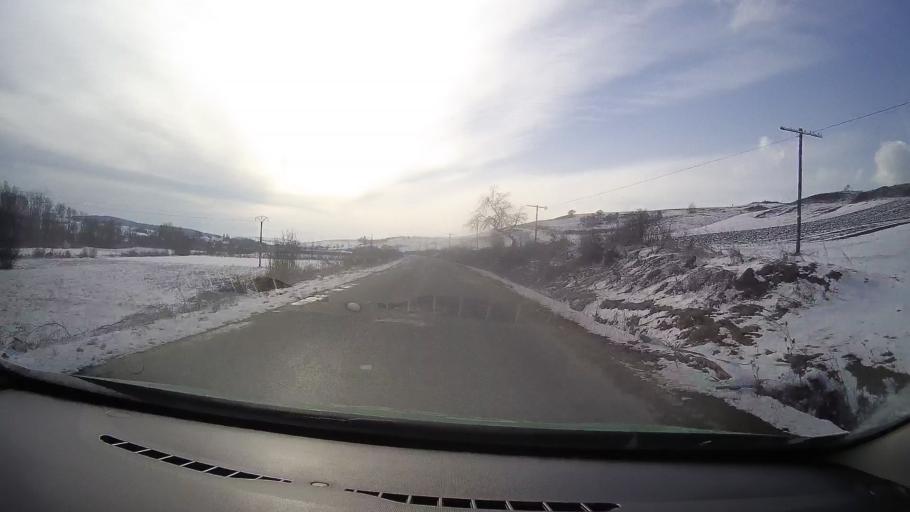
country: RO
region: Sibiu
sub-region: Oras Agnita
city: Ruja
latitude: 46.0152
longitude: 24.6915
